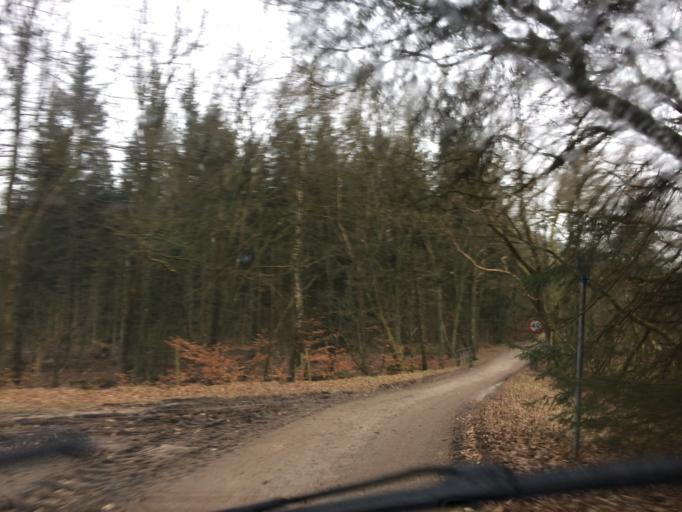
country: DK
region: Central Jutland
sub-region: Silkeborg Kommune
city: Virklund
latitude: 56.0283
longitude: 9.4946
